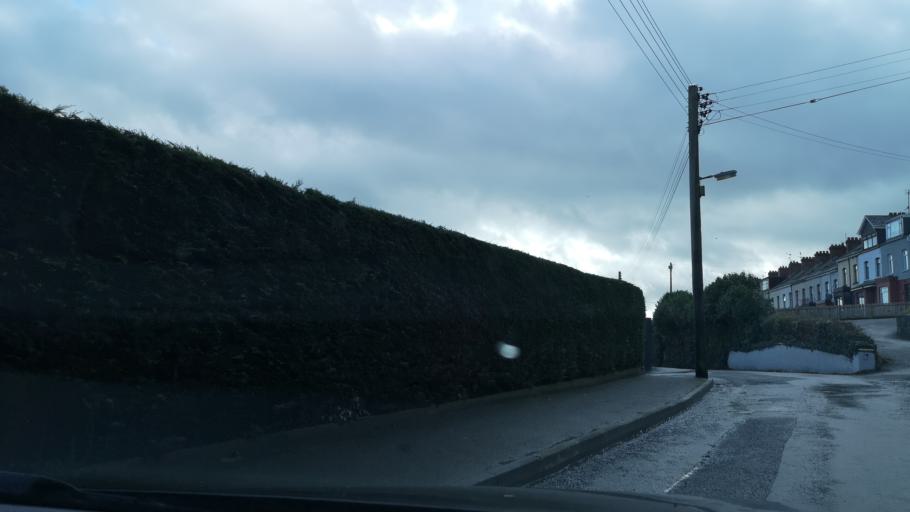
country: GB
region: Northern Ireland
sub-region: Newry and Mourne District
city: Newry
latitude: 54.1753
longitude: -6.3478
